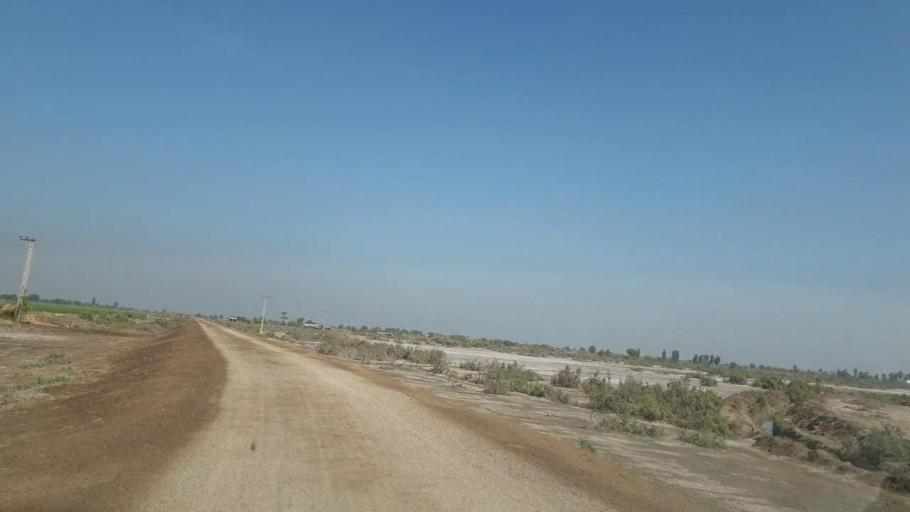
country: PK
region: Sindh
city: Mirpur Khas
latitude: 25.5688
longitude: 69.1850
